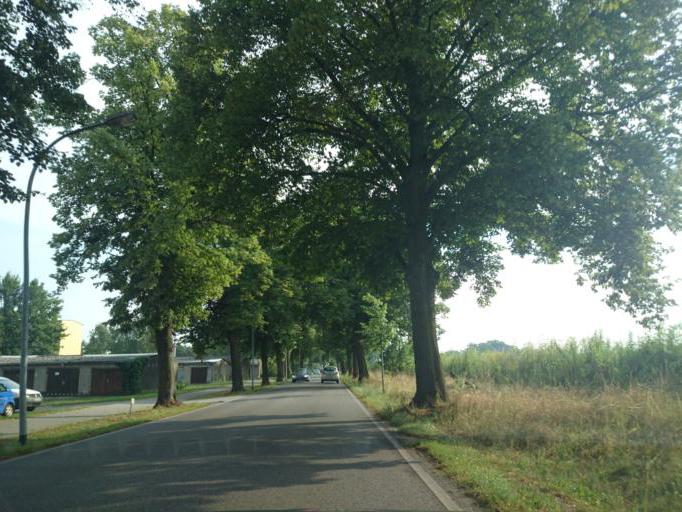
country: DE
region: Berlin
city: Lichtenrade
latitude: 52.3791
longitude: 13.4446
